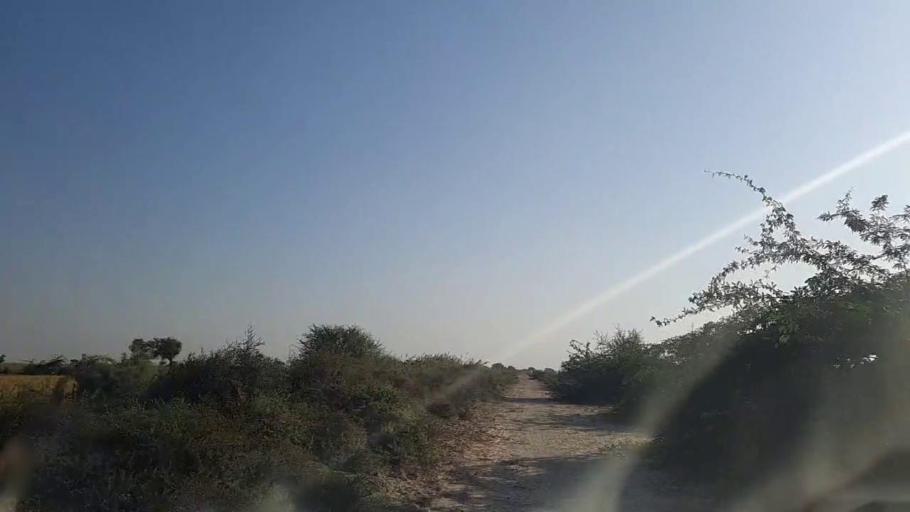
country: PK
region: Sindh
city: Jati
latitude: 24.3939
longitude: 68.2302
